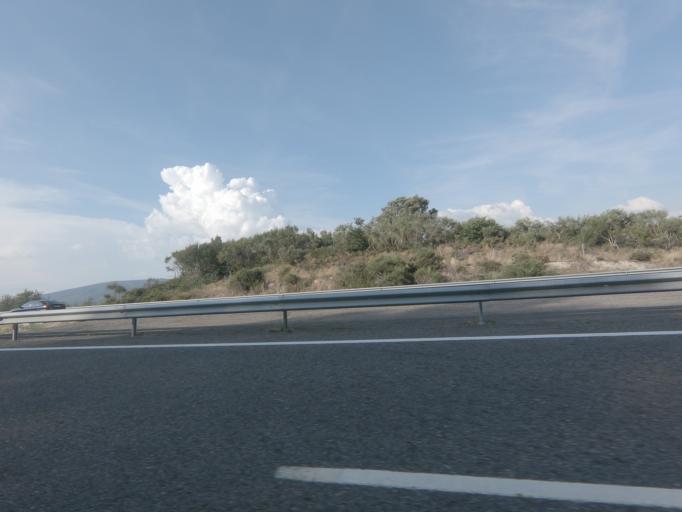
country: ES
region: Galicia
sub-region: Provincia de Ourense
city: Verin
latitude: 41.9600
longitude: -7.5147
